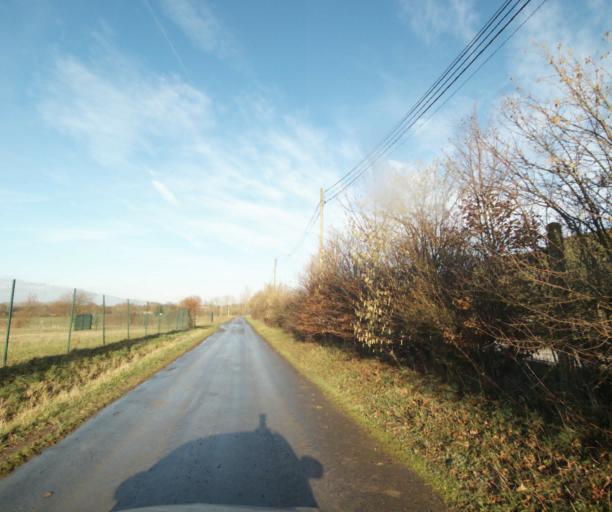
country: FR
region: Nord-Pas-de-Calais
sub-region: Departement du Nord
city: Curgies
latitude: 50.3185
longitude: 3.6007
